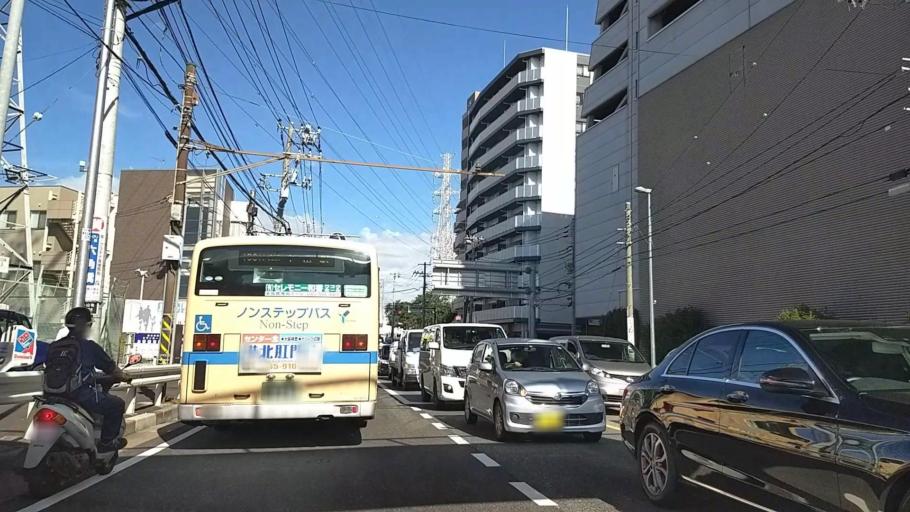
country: JP
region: Kanagawa
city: Yokohama
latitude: 35.5020
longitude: 139.6085
